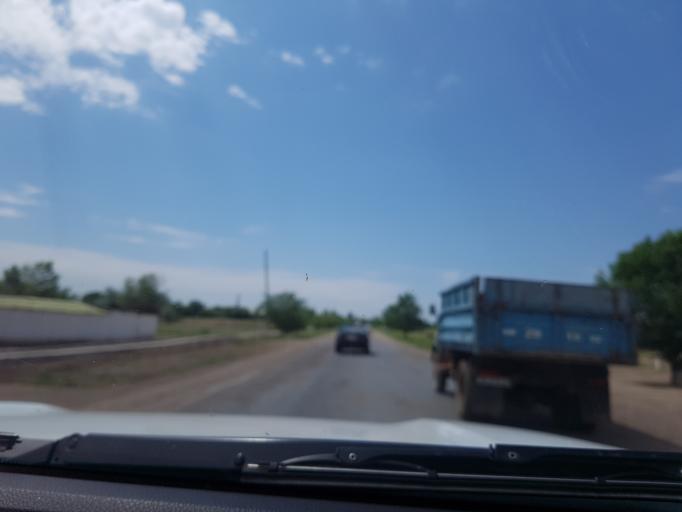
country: TM
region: Dasoguz
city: Koeneuergench
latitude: 42.3210
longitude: 59.1401
